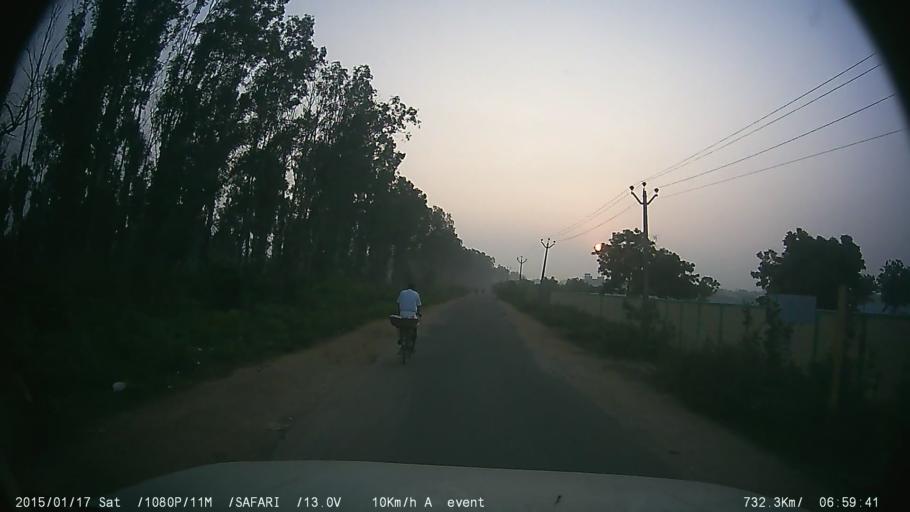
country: IN
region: Tamil Nadu
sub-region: Kancheepuram
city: Singapperumalkovil
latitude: 12.7977
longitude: 80.0100
